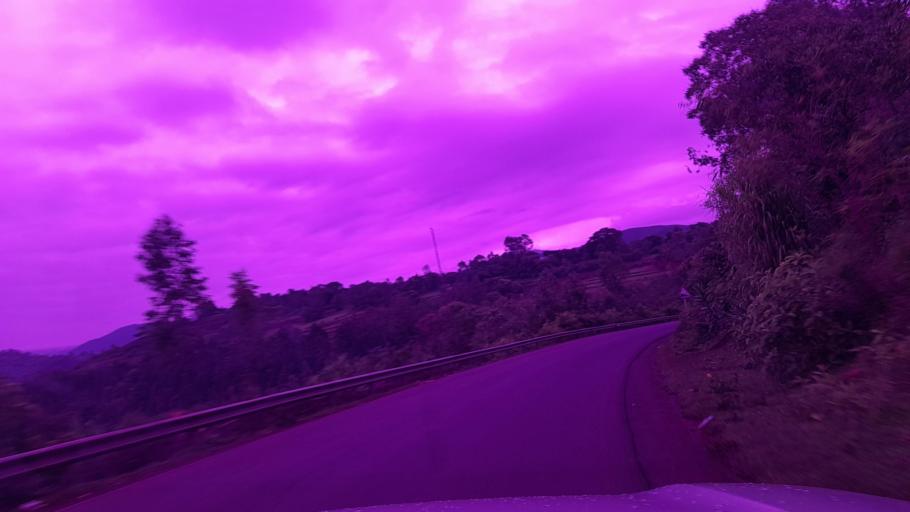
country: ET
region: Oromiya
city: Jima
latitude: 7.9286
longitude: 37.4311
